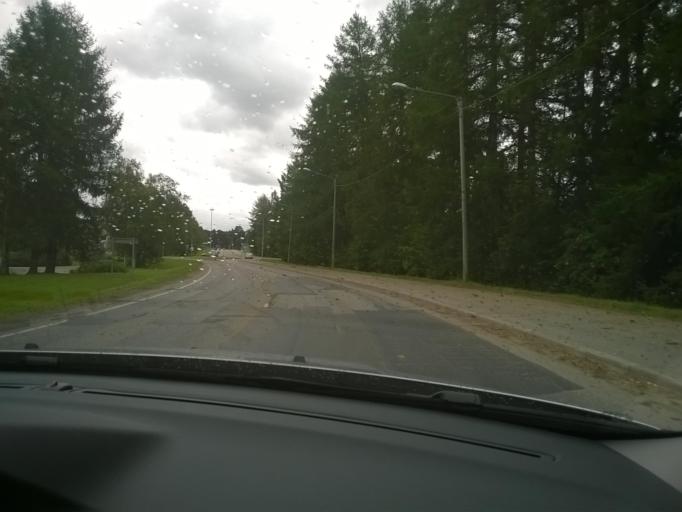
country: FI
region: Kainuu
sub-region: Kehys-Kainuu
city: Kuhmo
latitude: 64.1265
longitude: 29.5023
